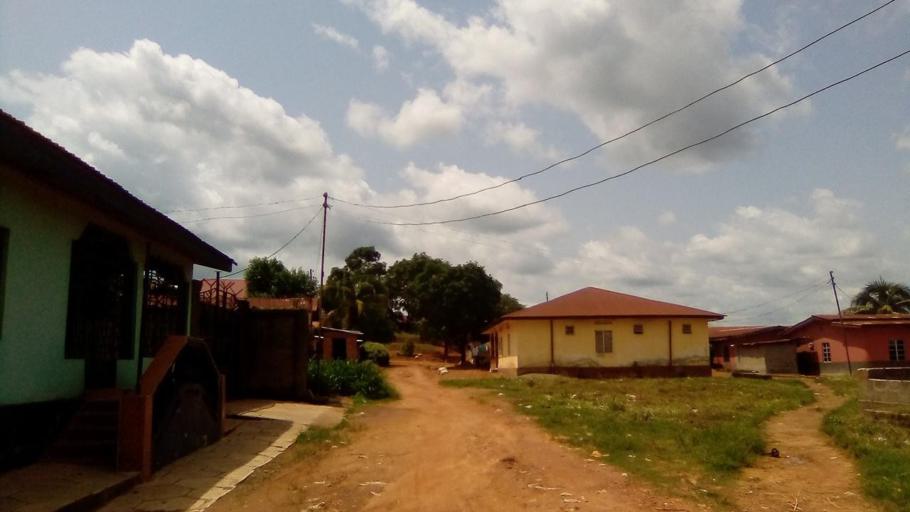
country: SL
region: Southern Province
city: Bo
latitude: 7.9671
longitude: -11.7283
